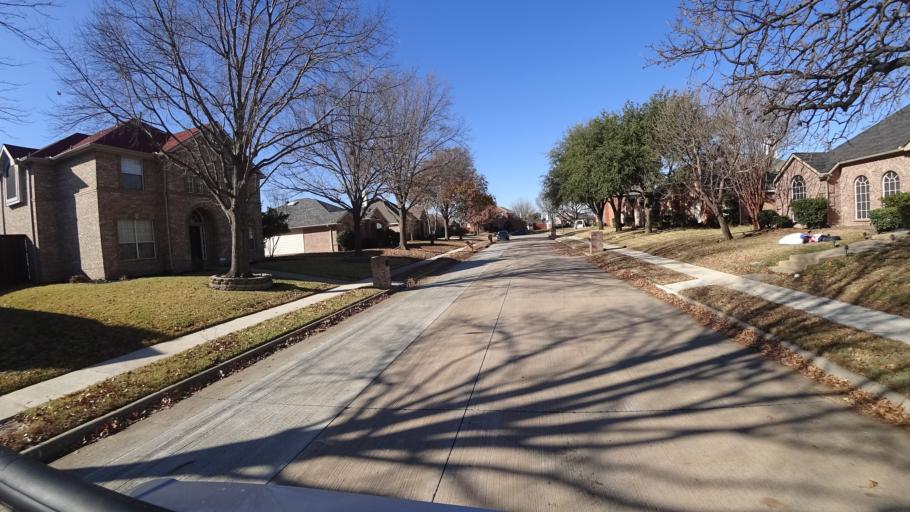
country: US
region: Texas
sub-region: Denton County
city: Lewisville
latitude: 33.0156
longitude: -97.0321
